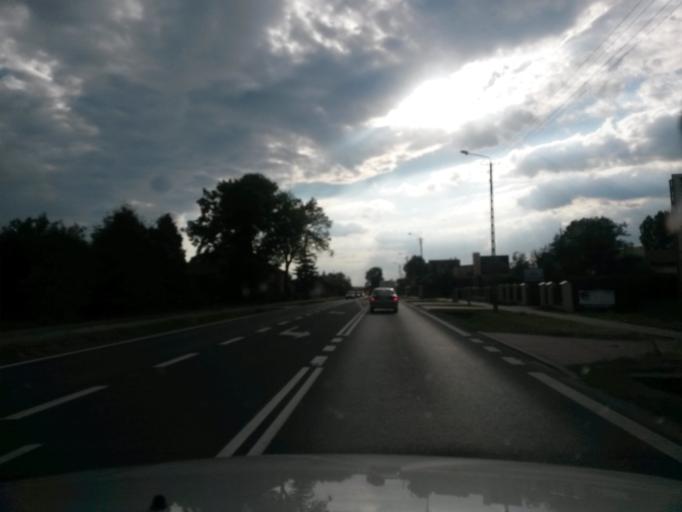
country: PL
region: Lodz Voivodeship
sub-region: Powiat piotrkowski
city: Wola Krzysztoporska
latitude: 51.4156
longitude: 19.5675
